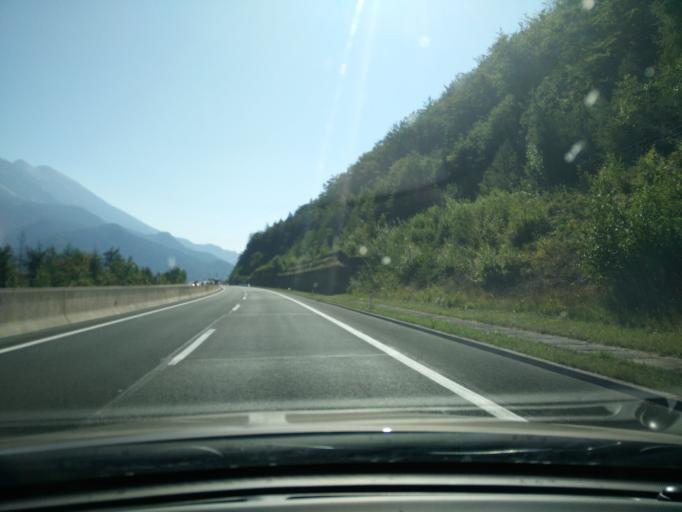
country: SI
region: Jesenice
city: Jesenice
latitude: 46.4285
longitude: 14.0596
